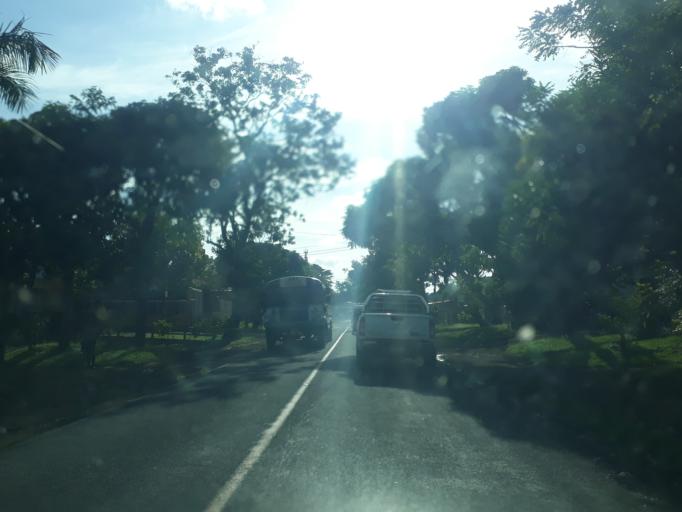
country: NI
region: Carazo
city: San Marcos
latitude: 11.9050
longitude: -86.1749
